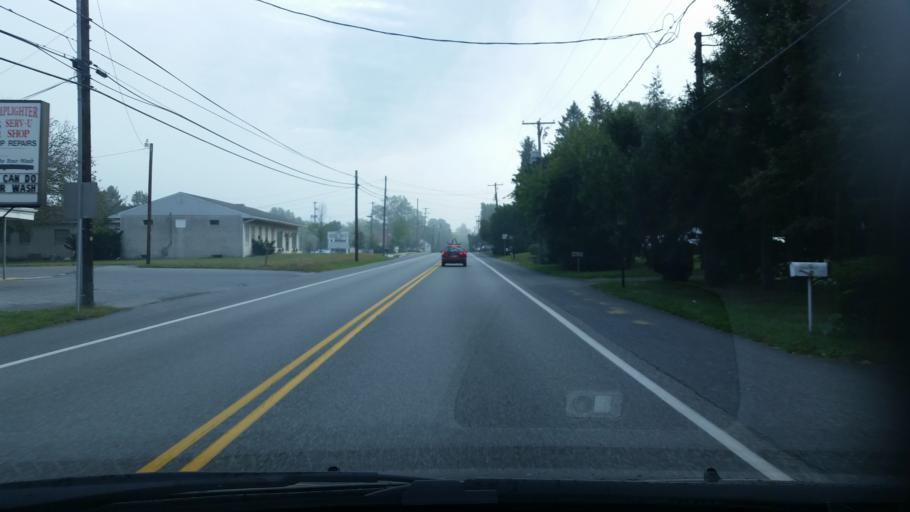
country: US
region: Pennsylvania
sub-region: Lancaster County
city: Brownstown
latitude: 40.0797
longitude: -76.2517
